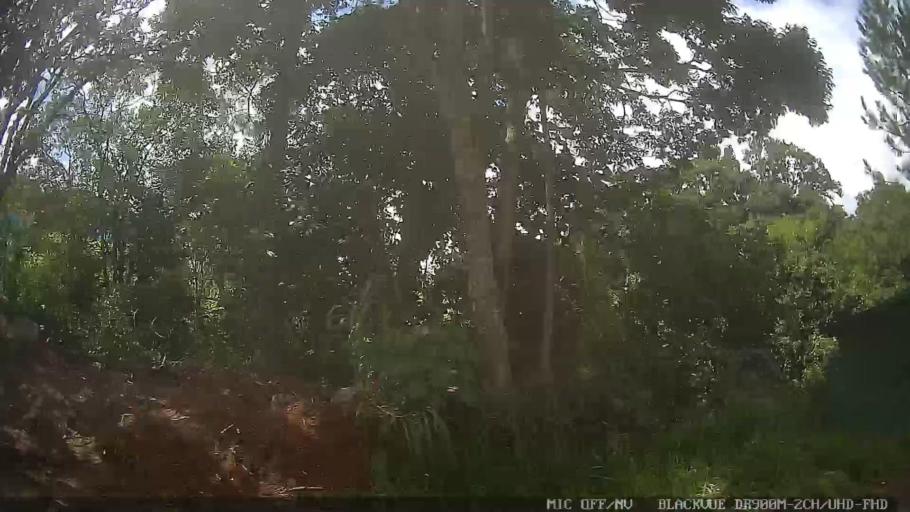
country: BR
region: Sao Paulo
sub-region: Braganca Paulista
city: Braganca Paulista
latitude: -22.8023
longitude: -46.4888
